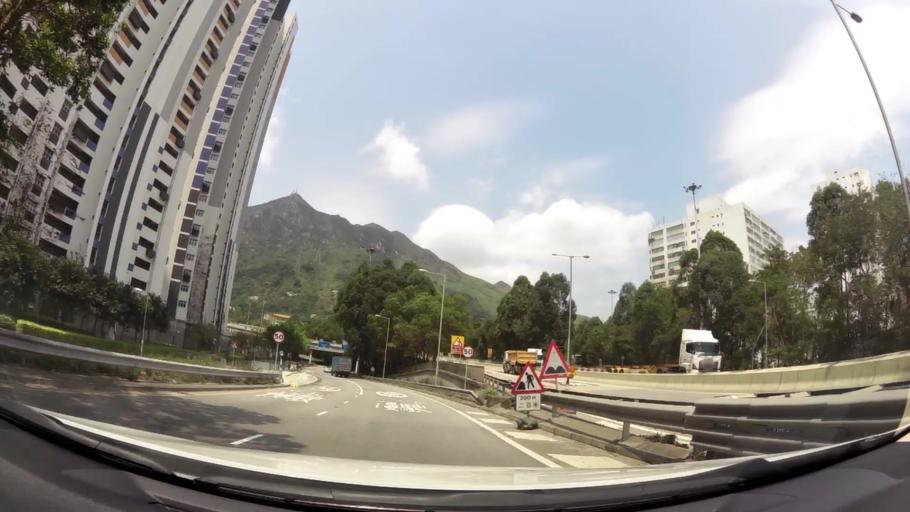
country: HK
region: Tuen Mun
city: Tuen Mun
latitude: 22.3871
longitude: 113.9685
